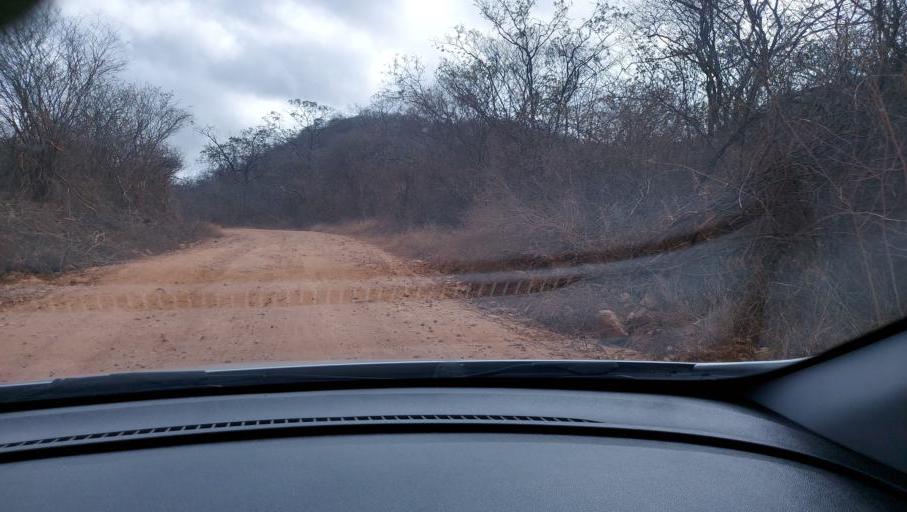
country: BR
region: Bahia
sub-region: Oliveira Dos Brejinhos
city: Beira Rio
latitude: -12.0928
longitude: -42.5430
